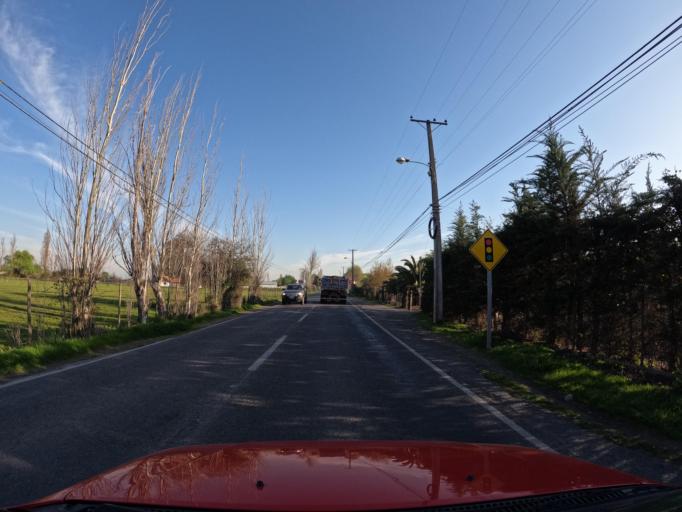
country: CL
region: Maule
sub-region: Provincia de Curico
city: Rauco
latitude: -34.8850
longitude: -71.2718
